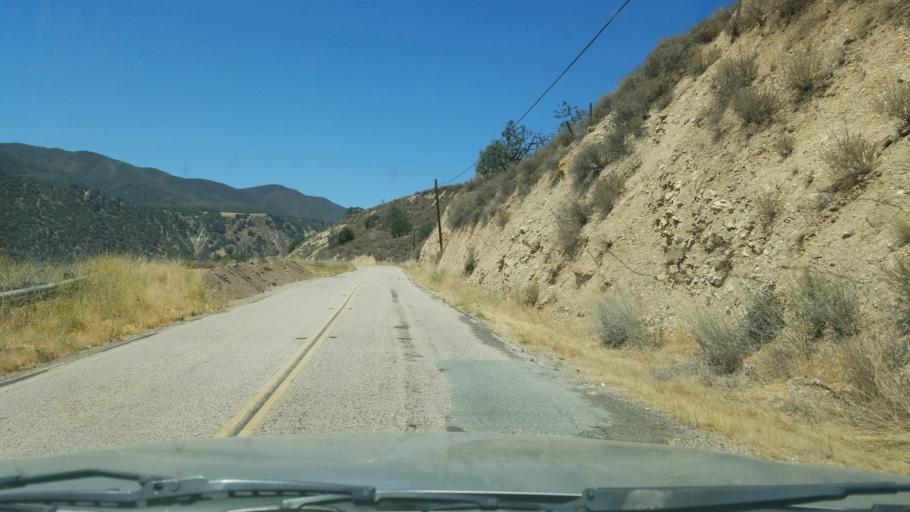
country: US
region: California
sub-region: Monterey County
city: Greenfield
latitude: 36.2682
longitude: -121.3566
